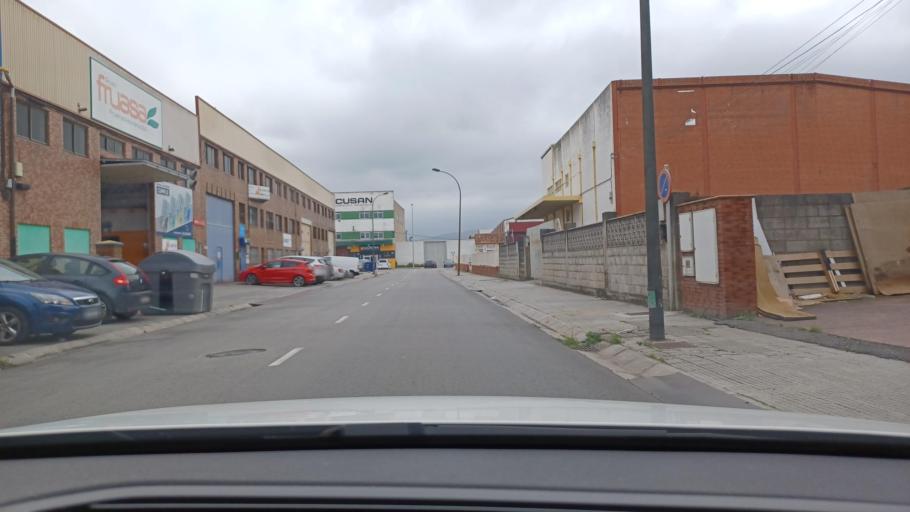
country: ES
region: Asturias
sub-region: Province of Asturias
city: Aviles
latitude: 43.5715
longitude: -5.9245
